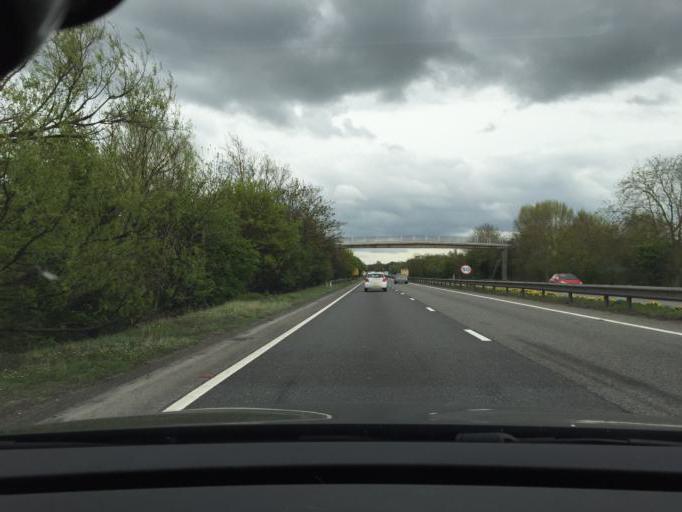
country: GB
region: England
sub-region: Oxfordshire
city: Harwell
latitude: 51.6279
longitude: -1.3098
